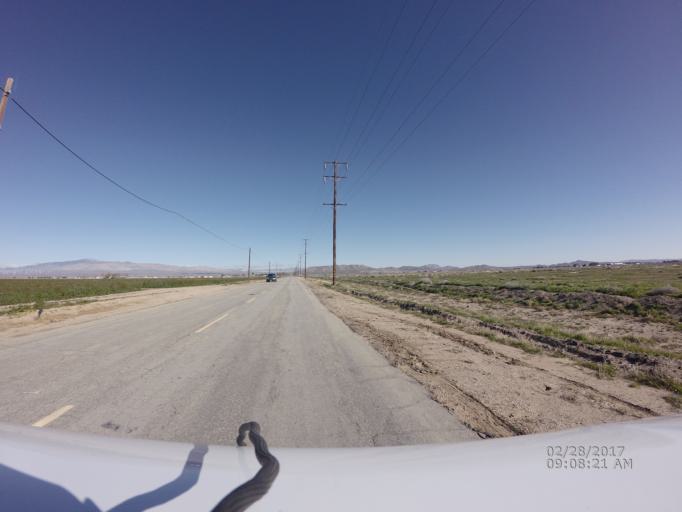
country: US
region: California
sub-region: Kern County
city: Rosamond
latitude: 34.8154
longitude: -118.2904
